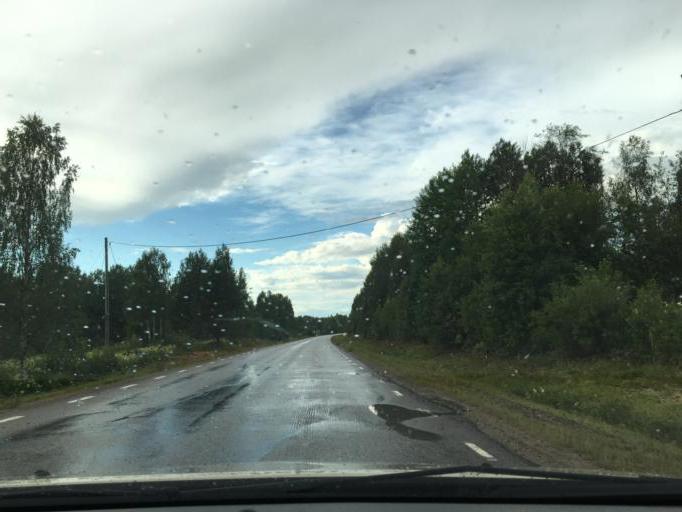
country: SE
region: Norrbotten
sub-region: Kalix Kommun
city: Toere
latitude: 66.0062
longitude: 22.8507
